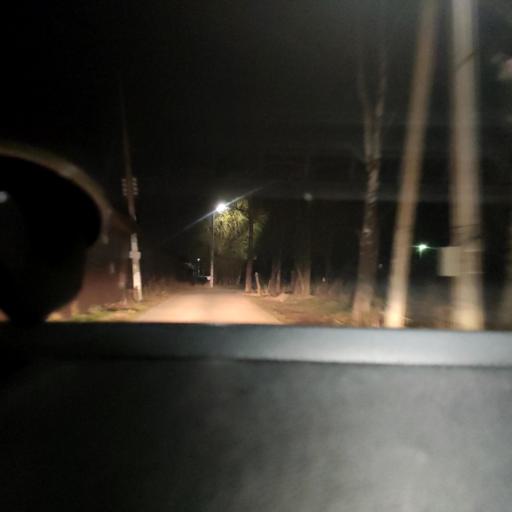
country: RU
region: Moskovskaya
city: Troitskoye
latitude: 55.2928
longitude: 38.4274
